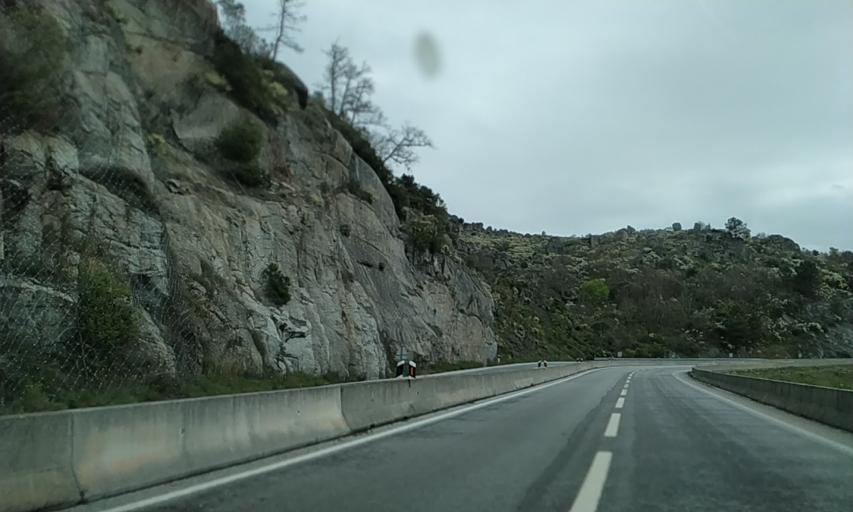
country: PT
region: Guarda
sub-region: Guarda
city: Guarda
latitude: 40.5949
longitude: -7.2754
